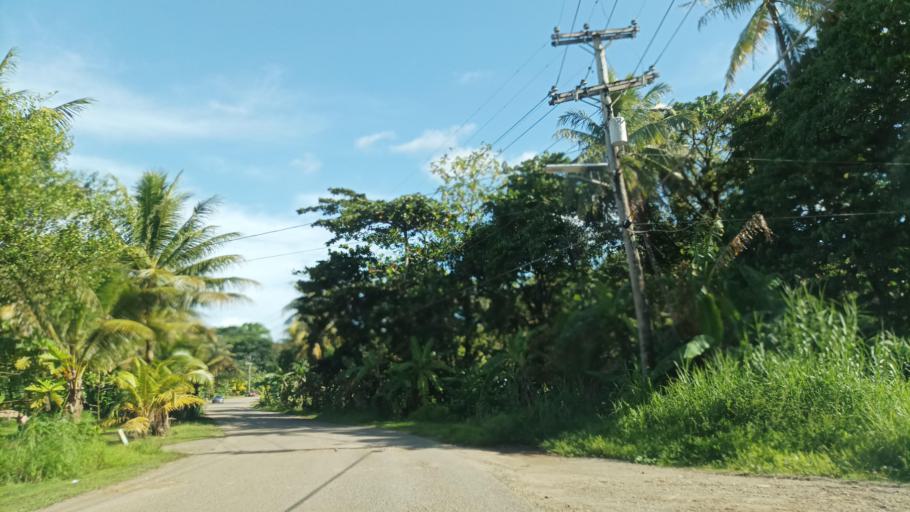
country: FM
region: Kosrae
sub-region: Lelu Municipality
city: Tofol
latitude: 5.3328
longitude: 163.0073
